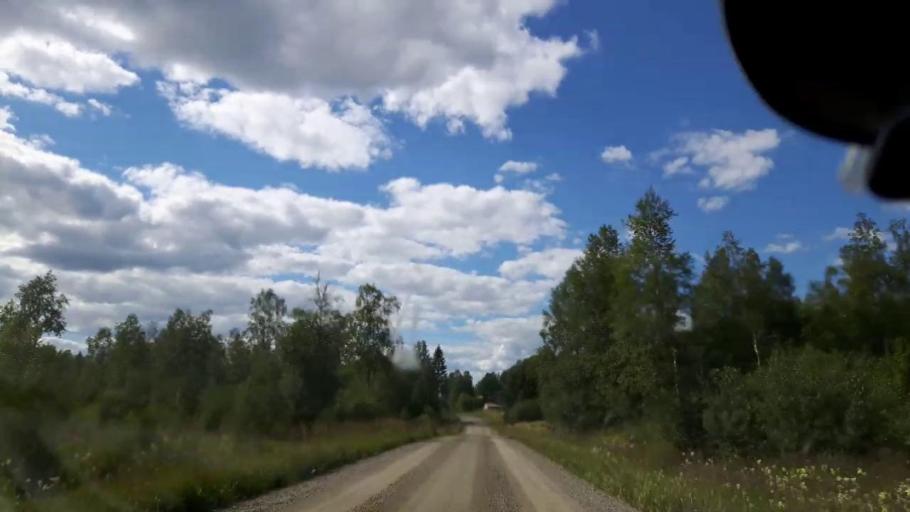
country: SE
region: Jaemtland
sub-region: Braecke Kommun
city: Braecke
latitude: 62.7235
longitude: 15.5417
